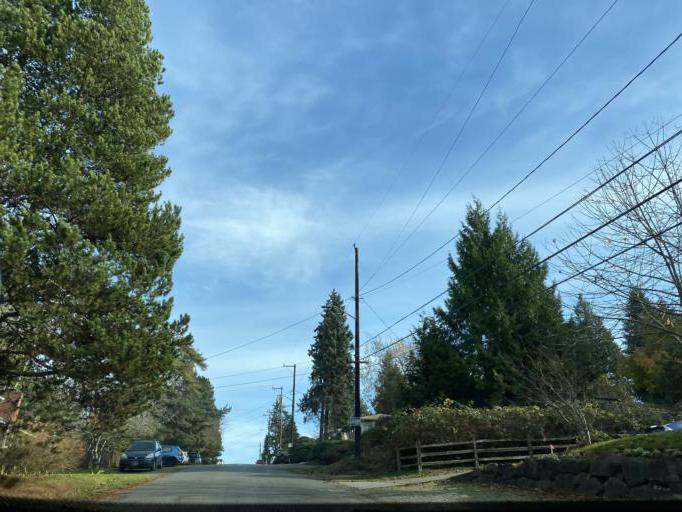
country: US
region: Washington
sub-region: King County
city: Lake Forest Park
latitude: 47.7002
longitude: -122.2966
